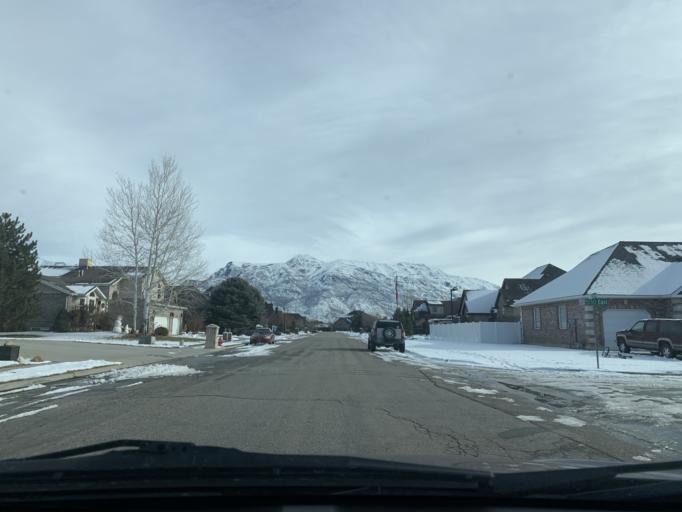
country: US
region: Utah
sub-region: Utah County
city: Lehi
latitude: 40.4105
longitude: -111.8252
